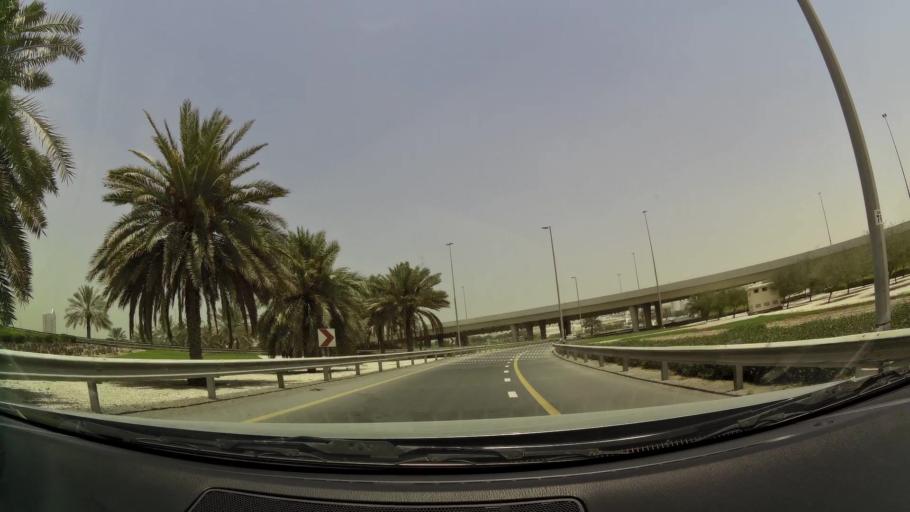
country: AE
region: Dubai
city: Dubai
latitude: 25.0575
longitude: 55.2500
